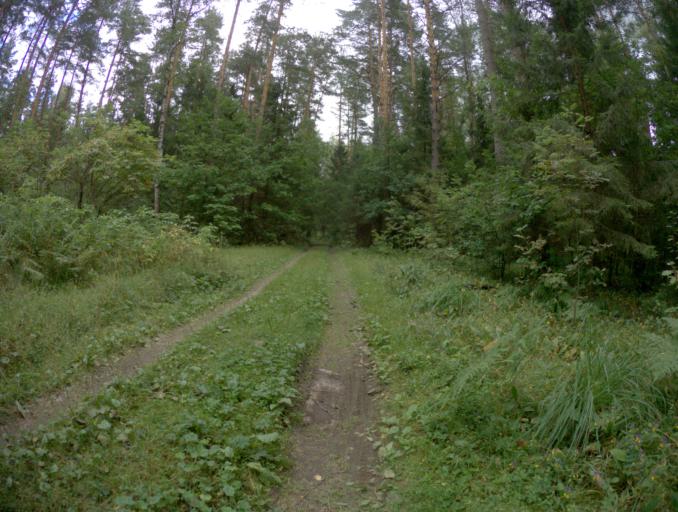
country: RU
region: Vladimir
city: Bogolyubovo
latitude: 56.1272
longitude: 40.5512
